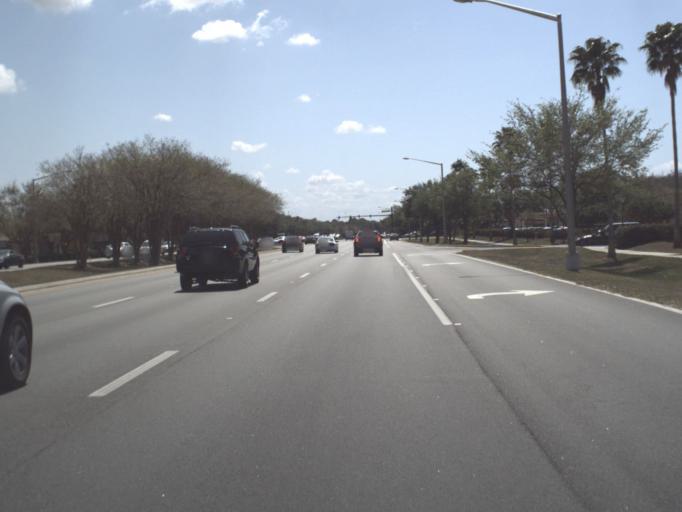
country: US
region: Florida
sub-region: Orange County
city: Hunters Creek
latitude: 28.3632
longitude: -81.4236
